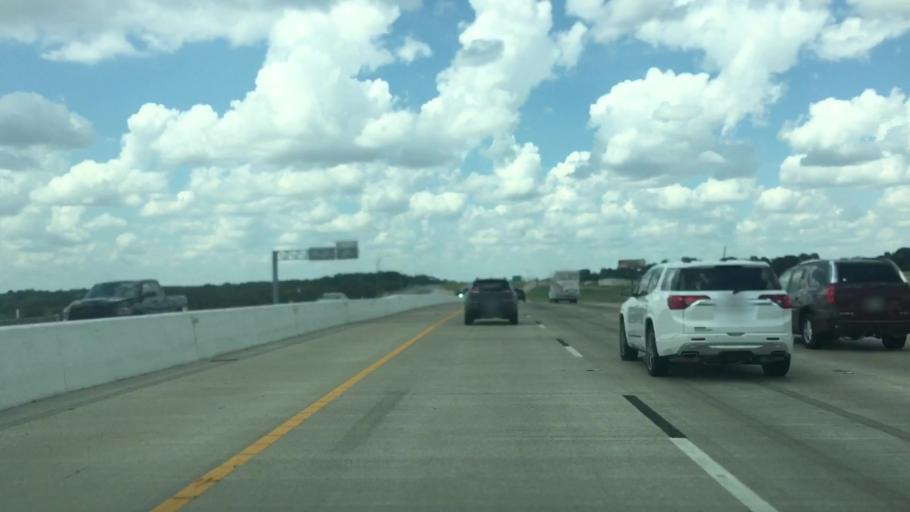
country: US
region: Texas
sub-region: McLennan County
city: West
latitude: 31.7287
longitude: -97.1030
